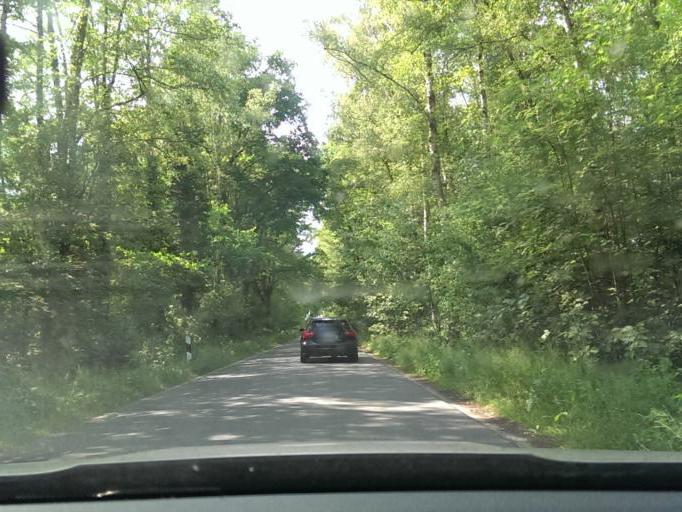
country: DE
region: Lower Saxony
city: Langenhagen
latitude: 52.5089
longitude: 9.7764
